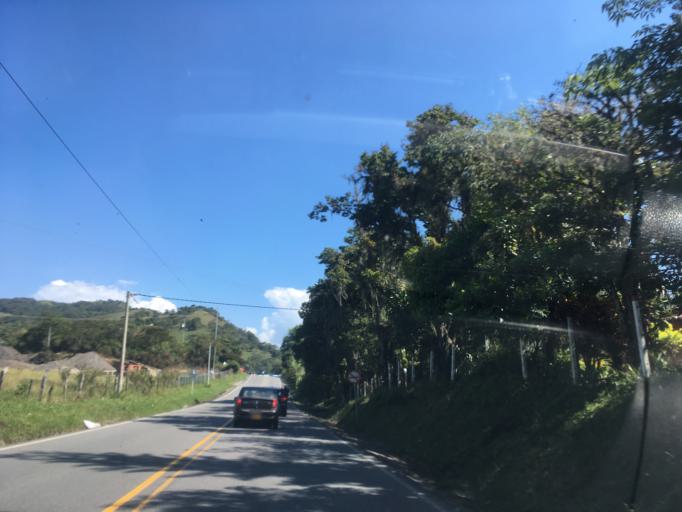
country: CO
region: Santander
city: Suaita
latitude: 6.0661
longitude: -73.4203
